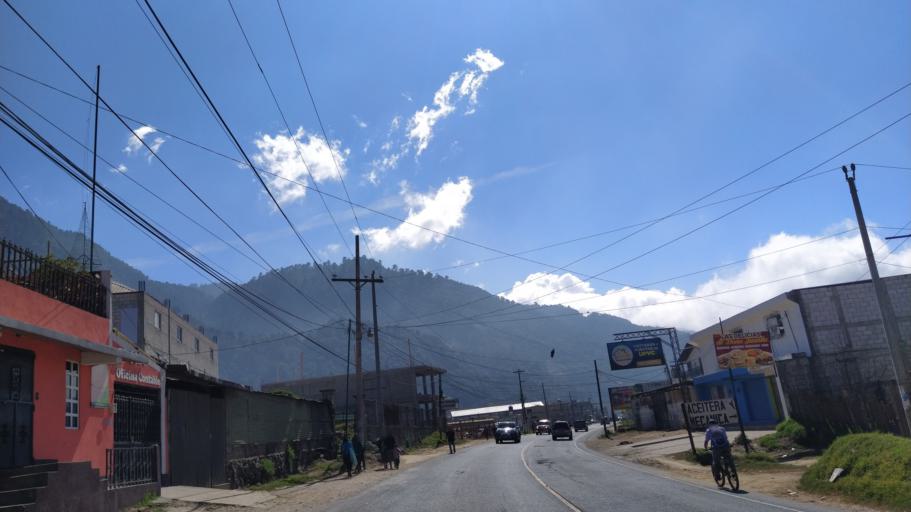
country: GT
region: Quetzaltenango
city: Cantel
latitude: 14.8074
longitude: -91.4476
